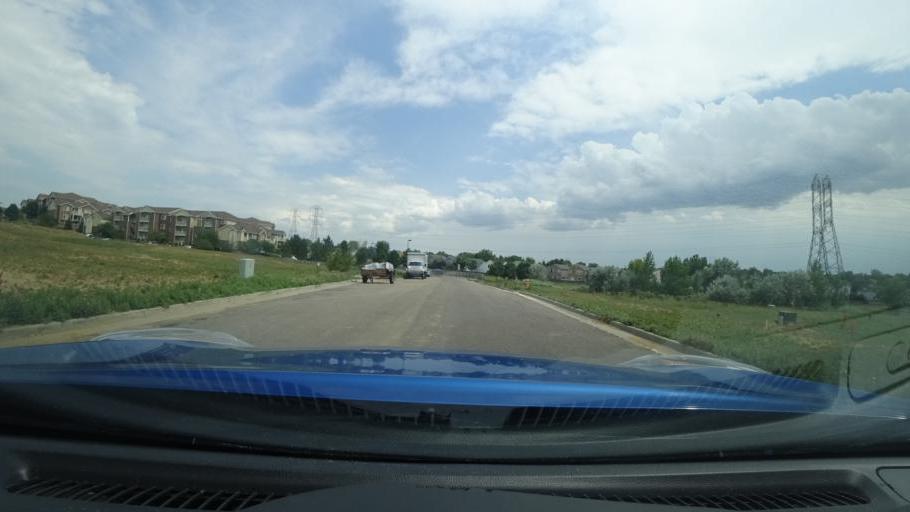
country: US
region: Colorado
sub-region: Adams County
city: Aurora
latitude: 39.6687
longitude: -104.7674
